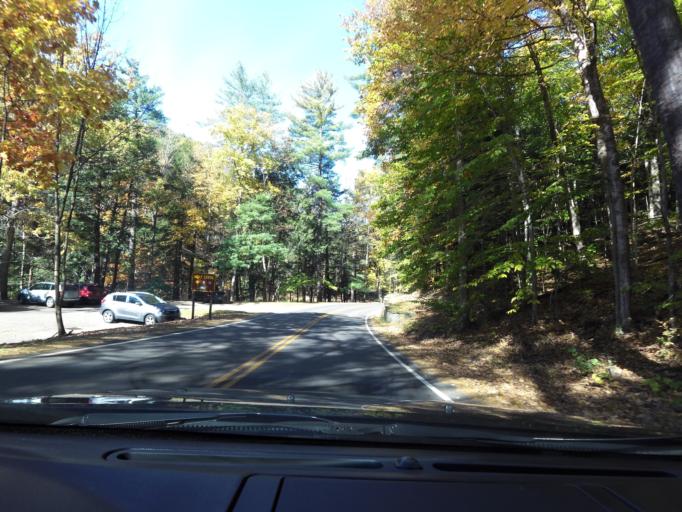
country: US
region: New York
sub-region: Wyoming County
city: Castile
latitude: 42.6147
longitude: -78.0110
